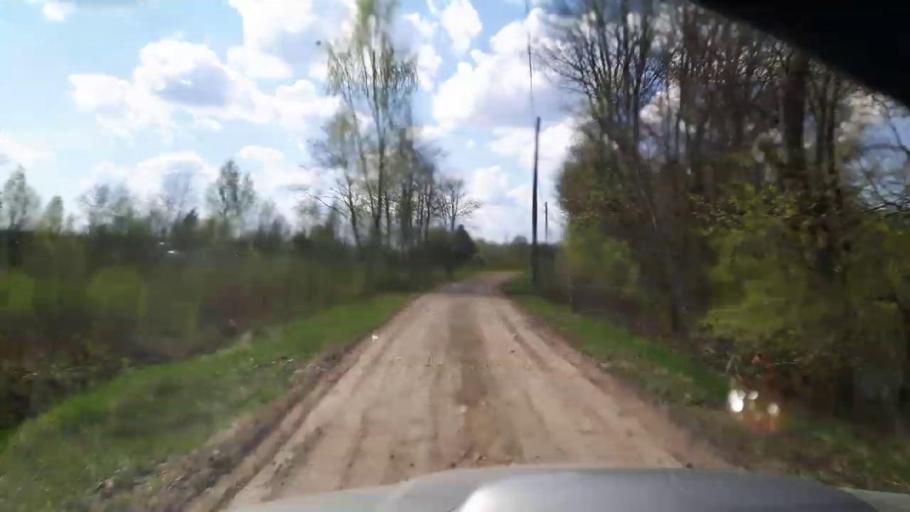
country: EE
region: Paernumaa
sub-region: Vaendra vald (alev)
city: Vandra
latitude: 58.4798
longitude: 24.9978
